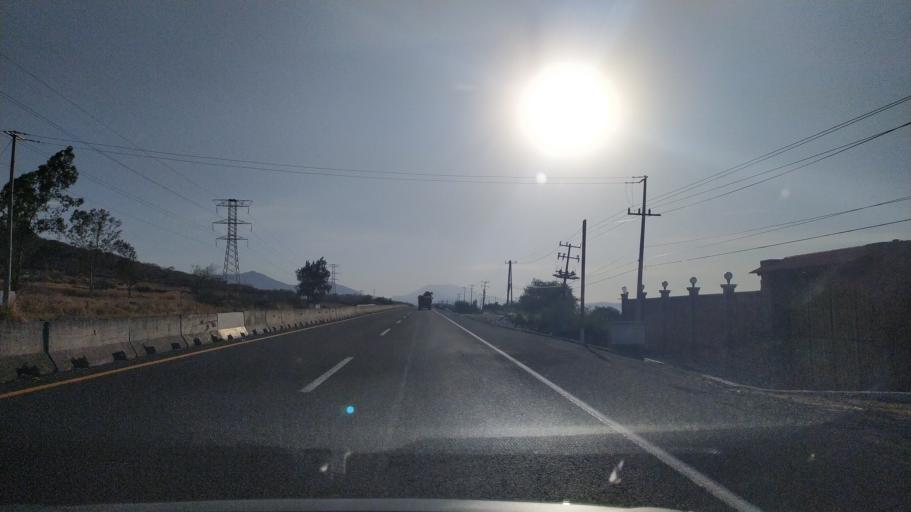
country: MX
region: Jalisco
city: Atotonilquillo
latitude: 20.3959
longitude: -103.0880
